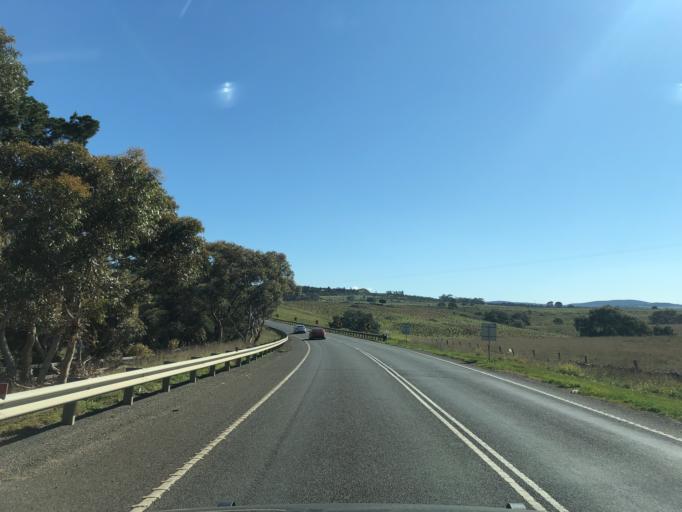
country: AU
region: Victoria
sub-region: Hume
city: Diggers Rest
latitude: -37.6249
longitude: 144.6620
